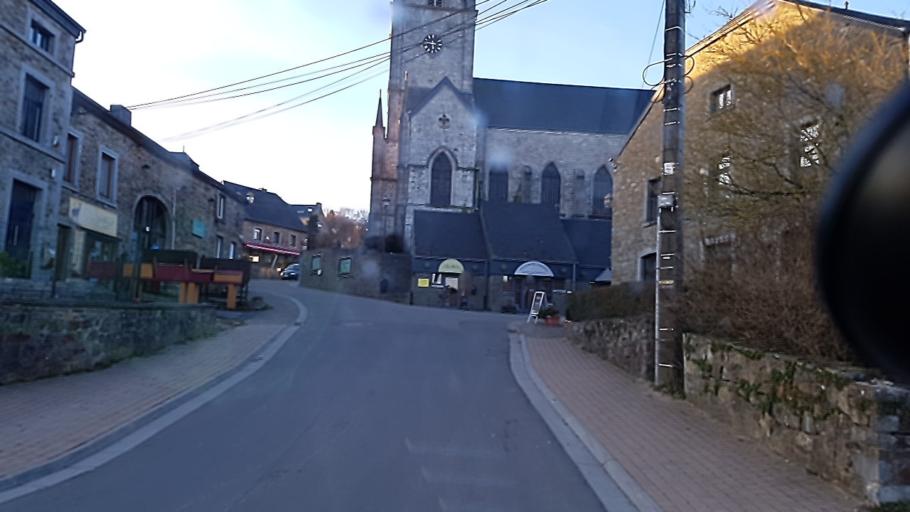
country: BE
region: Wallonia
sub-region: Province du Luxembourg
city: Daverdisse
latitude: 50.0067
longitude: 5.1603
